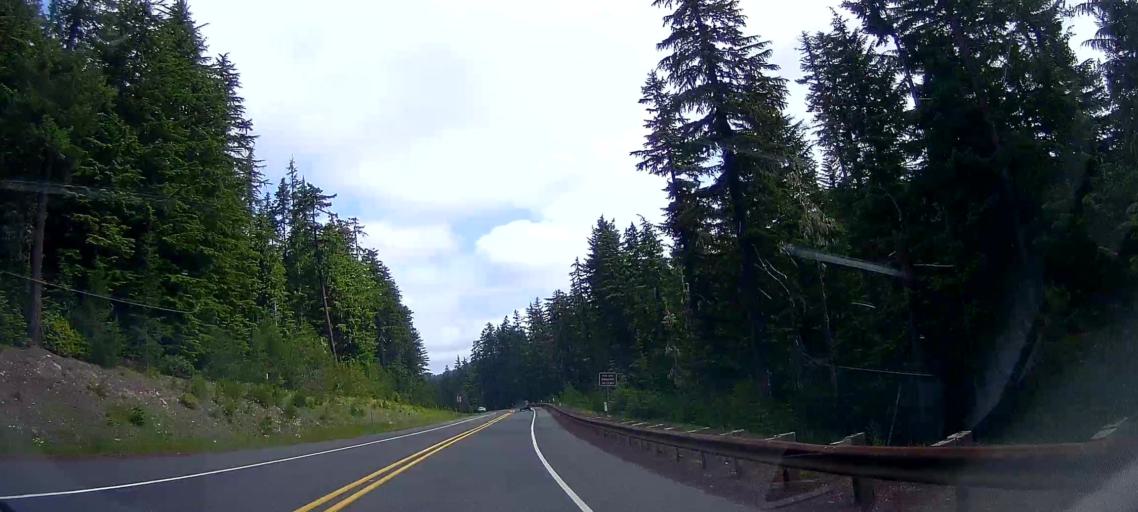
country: US
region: Oregon
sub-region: Clackamas County
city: Mount Hood Village
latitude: 45.2214
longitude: -121.6984
